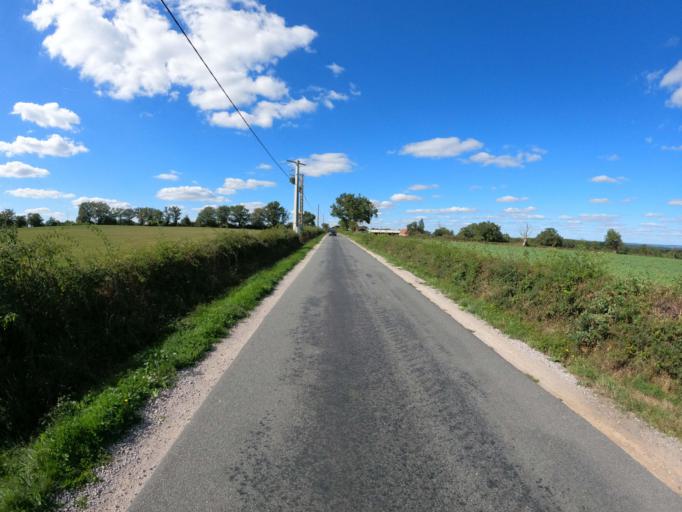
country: FR
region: Auvergne
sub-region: Departement de l'Allier
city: Doyet
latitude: 46.3986
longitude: 2.7494
